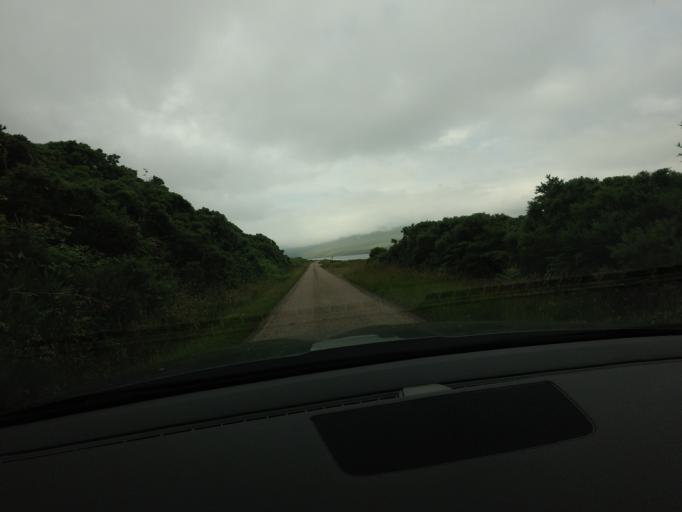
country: GB
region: Scotland
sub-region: Highland
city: Golspie
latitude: 58.3790
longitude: -4.3652
